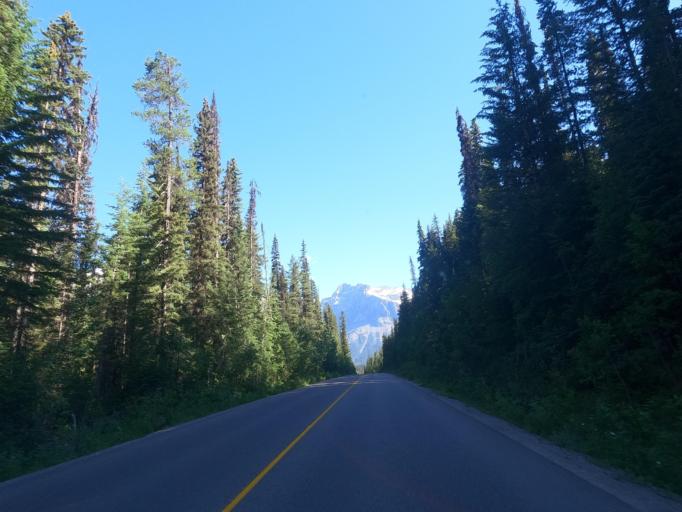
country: CA
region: Alberta
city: Lake Louise
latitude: 51.4134
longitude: -116.5335
